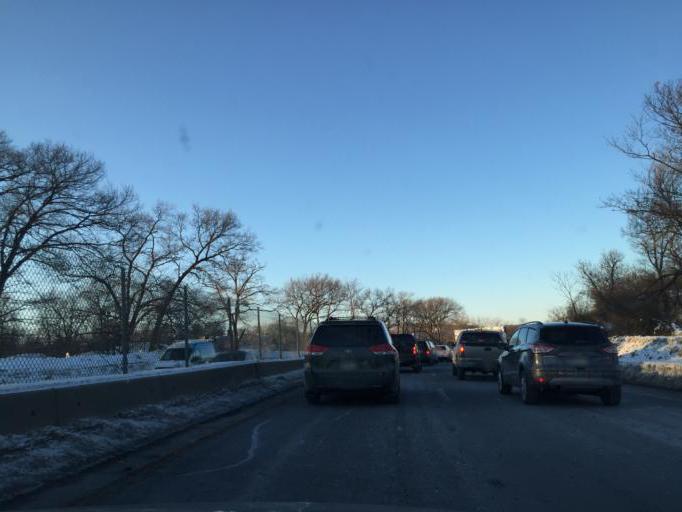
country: US
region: Massachusetts
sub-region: Essex County
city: Saugus
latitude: 42.4400
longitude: -71.0281
